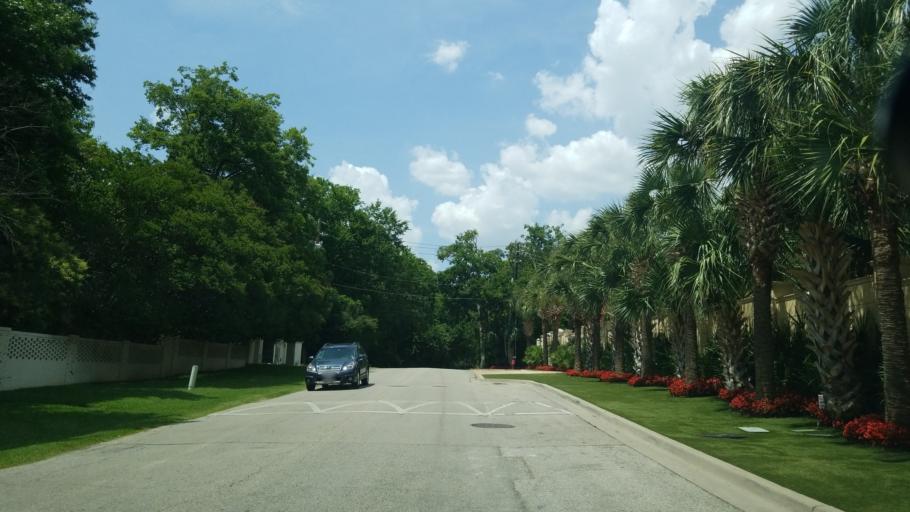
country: US
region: Texas
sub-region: Dallas County
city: University Park
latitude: 32.8691
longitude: -96.8086
